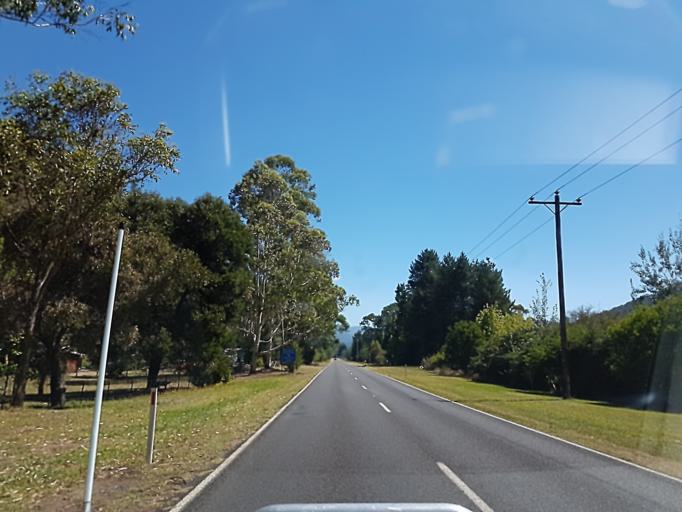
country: AU
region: Victoria
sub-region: Alpine
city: Mount Beauty
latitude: -36.7784
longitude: 147.0332
